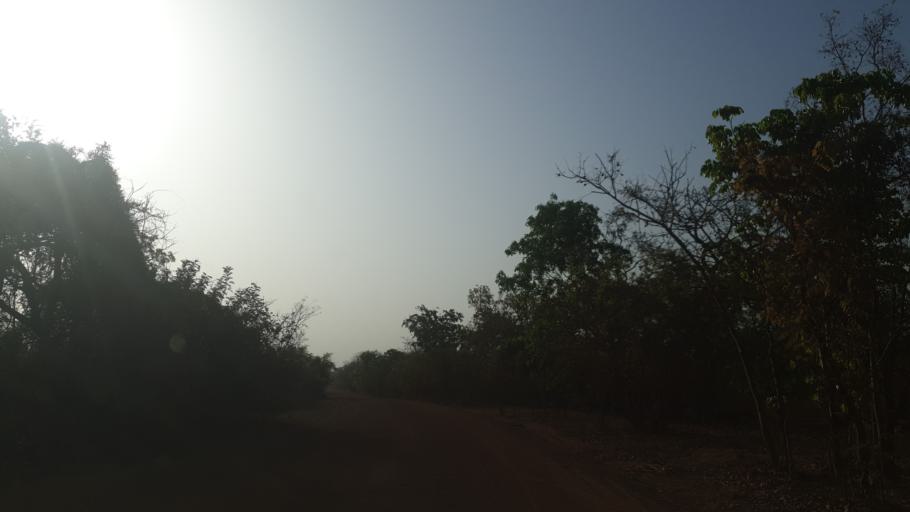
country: ML
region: Sikasso
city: Kolondieba
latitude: 10.8981
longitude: -6.8878
